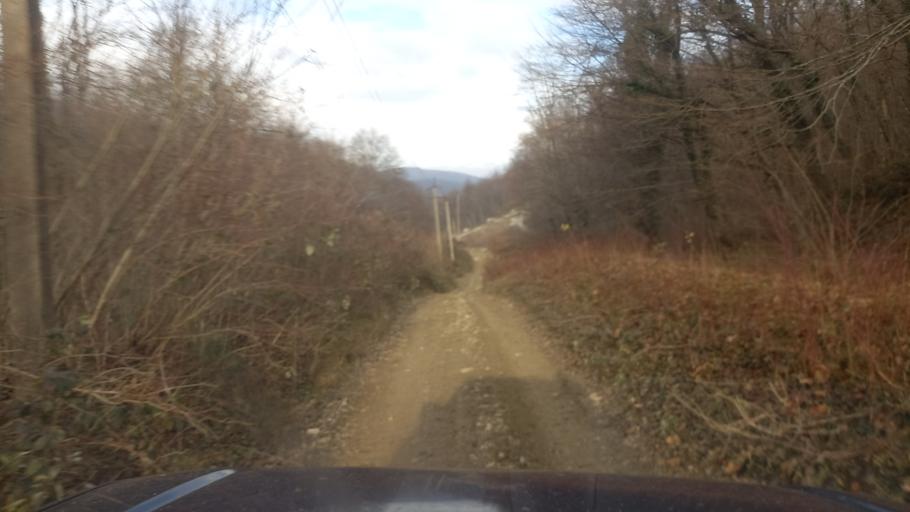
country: RU
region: Krasnodarskiy
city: Neftegorsk
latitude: 44.2095
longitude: 39.7100
